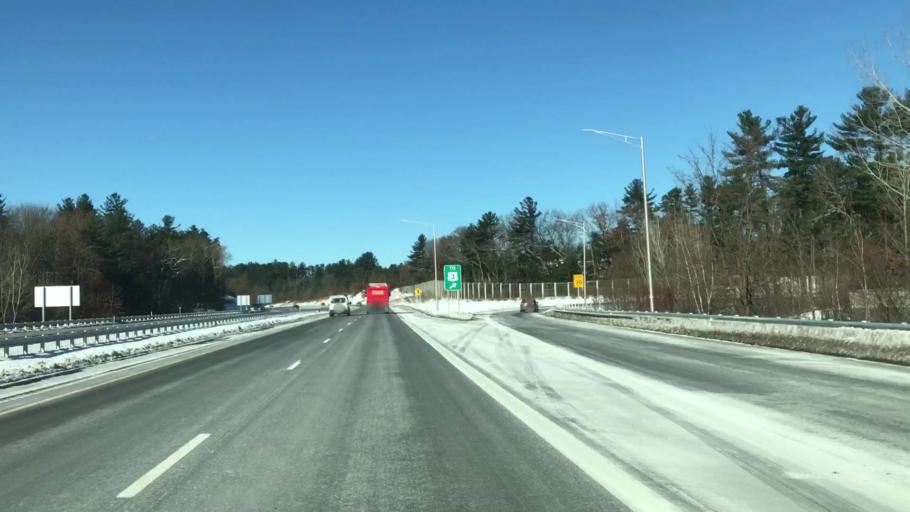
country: US
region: New Hampshire
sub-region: Hillsborough County
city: Bedford
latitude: 42.9552
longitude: -71.4851
